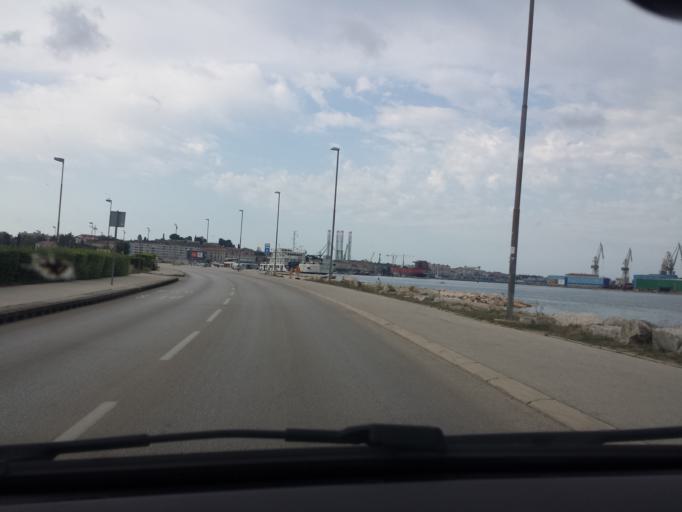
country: HR
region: Istarska
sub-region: Grad Pula
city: Pula
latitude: 44.8800
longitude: 13.8465
